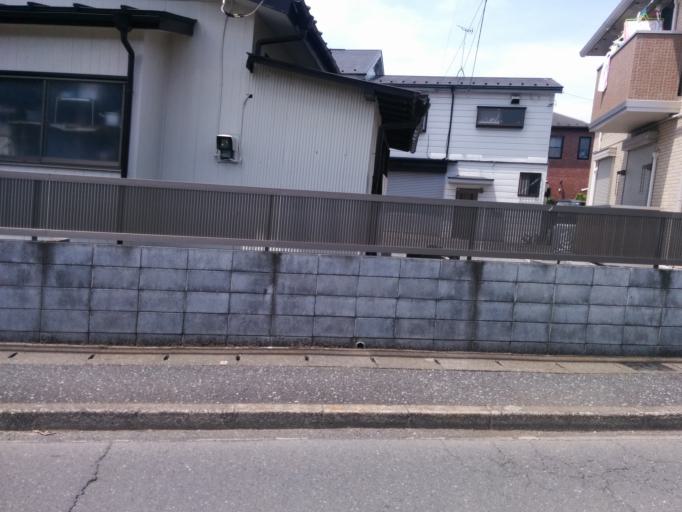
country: JP
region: Tokyo
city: Higashimurayama-shi
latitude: 35.7549
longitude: 139.4807
